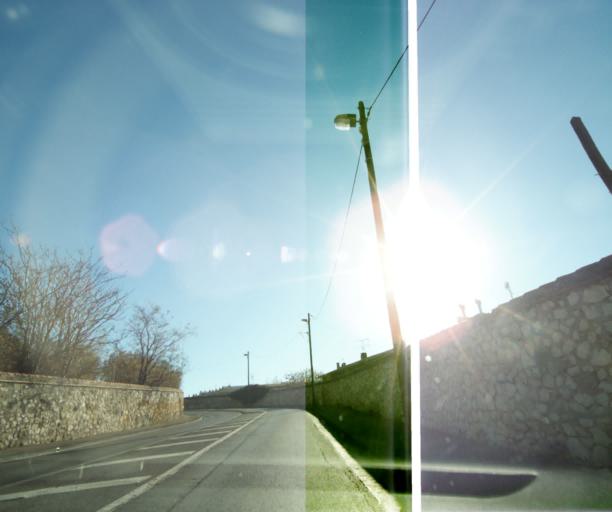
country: FR
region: Provence-Alpes-Cote d'Azur
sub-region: Departement des Bouches-du-Rhone
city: Marseille 15
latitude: 43.3501
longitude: 5.3542
